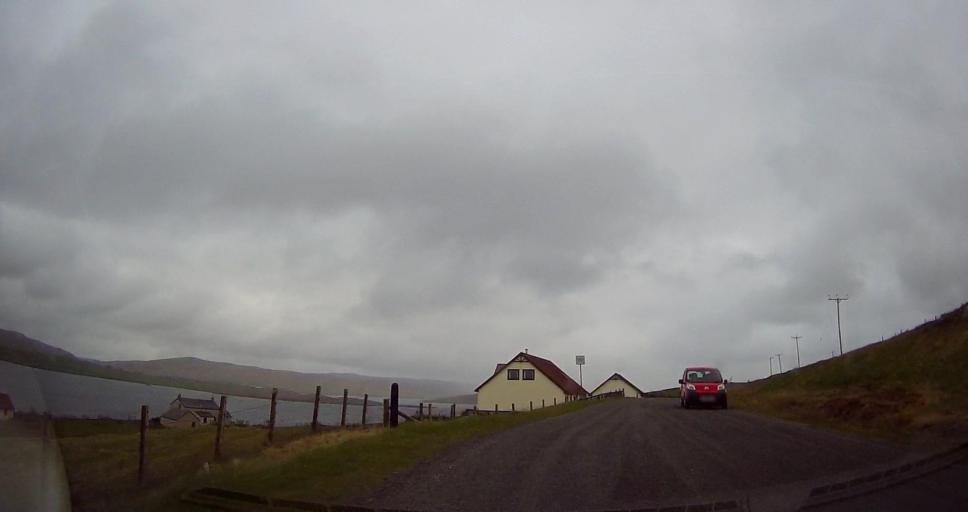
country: GB
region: Scotland
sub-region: Shetland Islands
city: Lerwick
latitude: 60.3836
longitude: -1.3794
